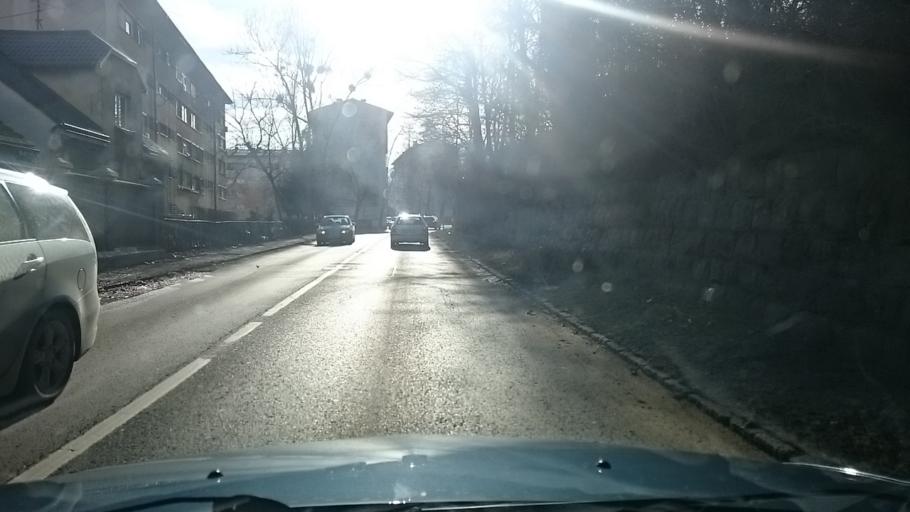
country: BA
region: Republika Srpska
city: Hiseti
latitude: 44.7678
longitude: 17.1804
